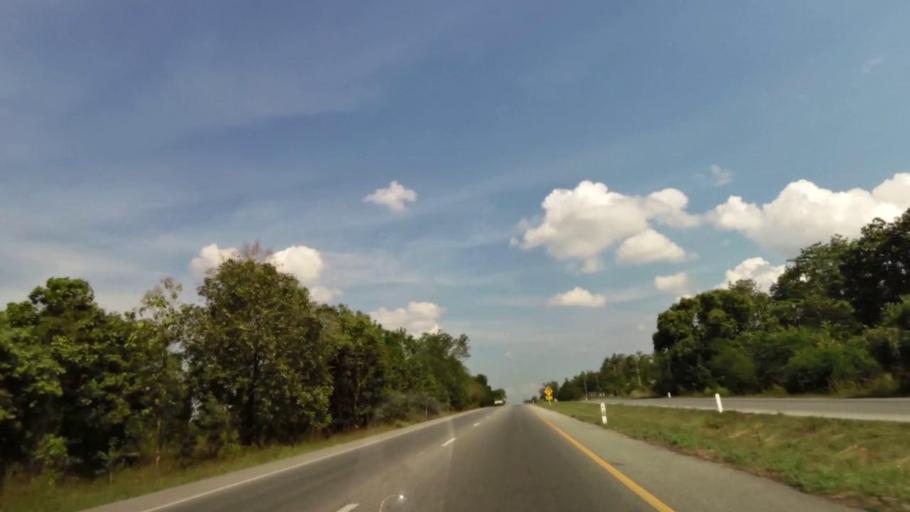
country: TH
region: Uttaradit
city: Thong Saen Khan
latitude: 17.4475
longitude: 100.2348
